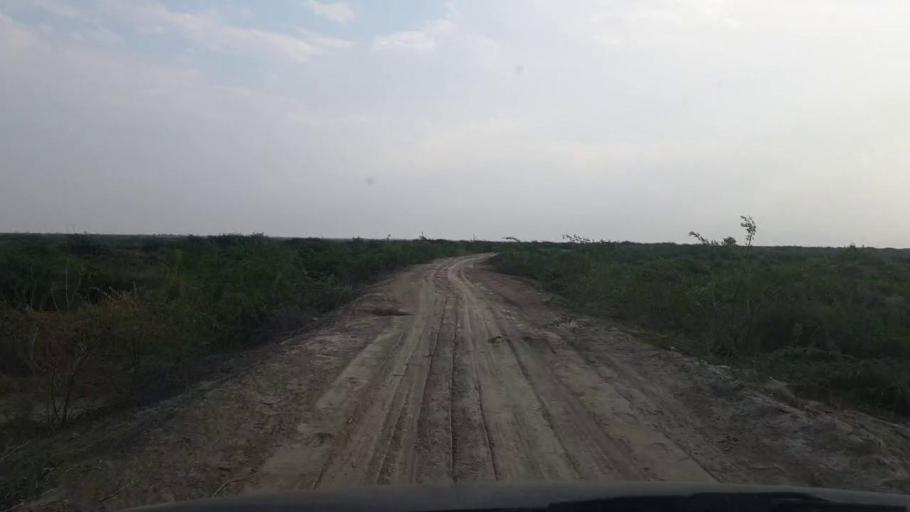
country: PK
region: Sindh
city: Badin
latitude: 24.4777
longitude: 68.6998
